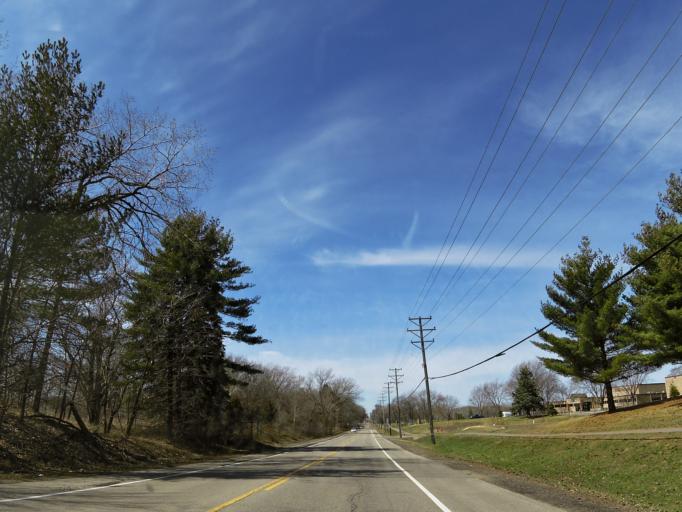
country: US
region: Minnesota
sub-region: Ramsey County
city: North Saint Paul
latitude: 44.9924
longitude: -92.9875
